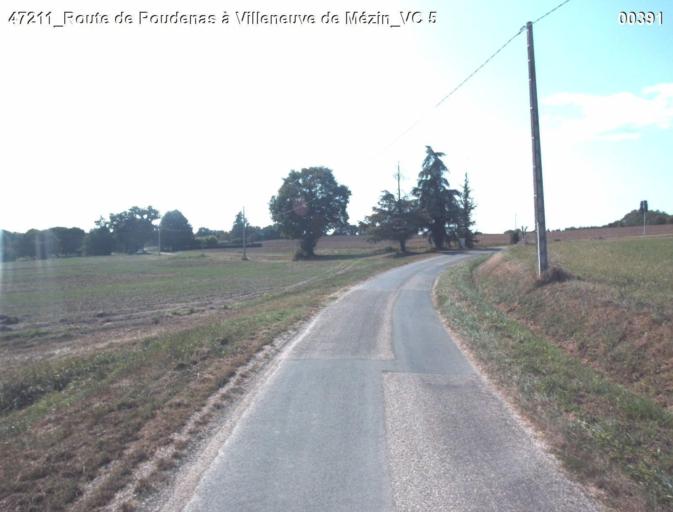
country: FR
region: Aquitaine
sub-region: Departement du Lot-et-Garonne
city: Mezin
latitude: 44.0377
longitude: 0.2201
